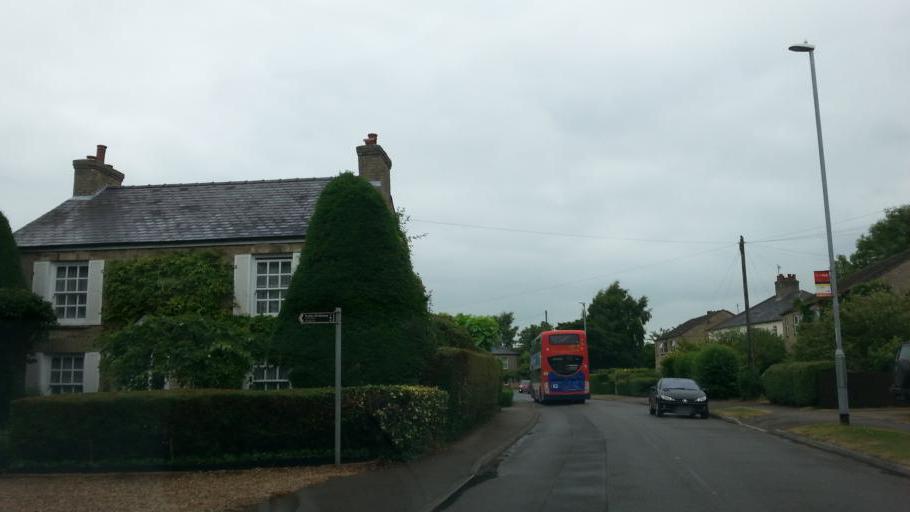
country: GB
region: England
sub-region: Cambridgeshire
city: Histon
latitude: 52.2579
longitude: 0.1035
